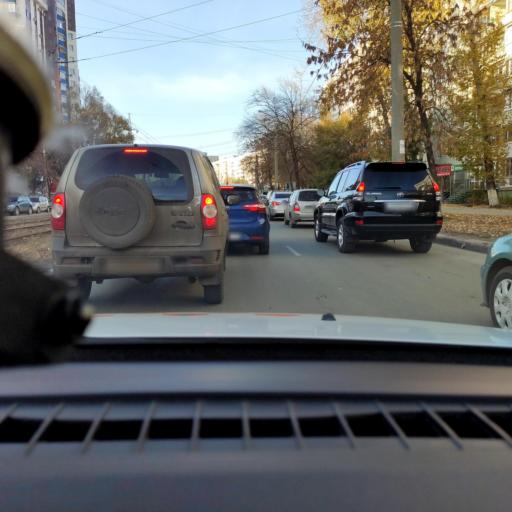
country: RU
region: Samara
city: Samara
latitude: 53.2414
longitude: 50.2123
